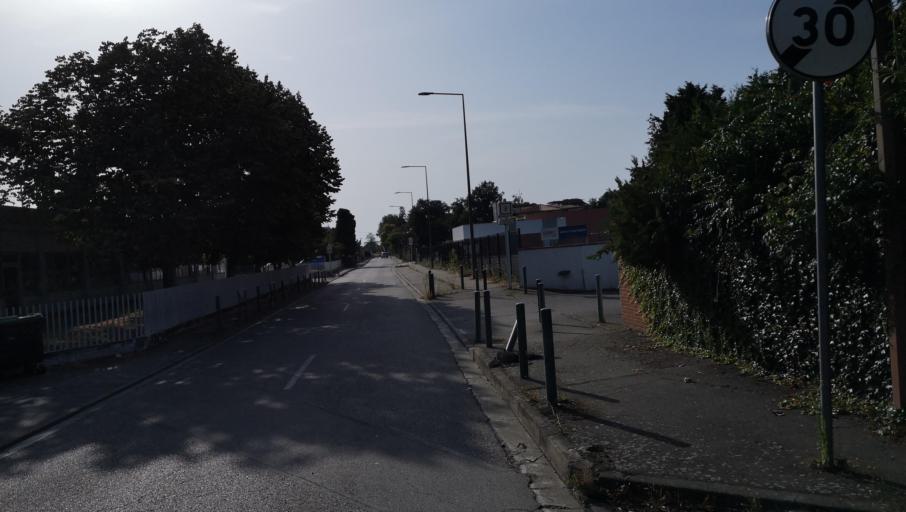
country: FR
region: Midi-Pyrenees
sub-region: Departement de la Haute-Garonne
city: Cugnaux
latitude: 43.5677
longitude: 1.3820
